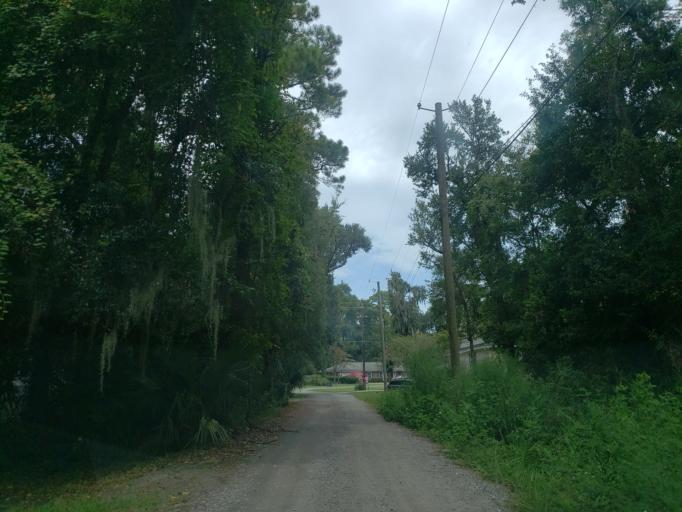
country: US
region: Georgia
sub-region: Chatham County
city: Wilmington Island
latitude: 32.0038
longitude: -80.9653
